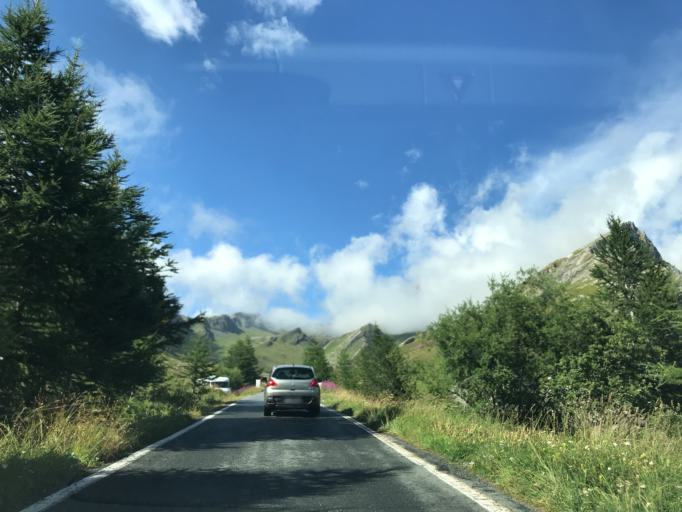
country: IT
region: Piedmont
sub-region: Provincia di Cuneo
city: Pontechianale
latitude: 44.6592
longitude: 6.9861
